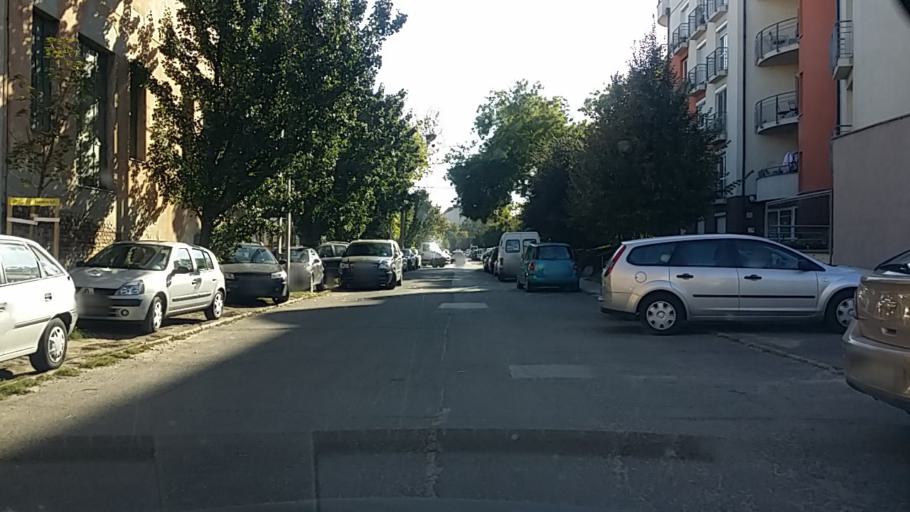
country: HU
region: Budapest
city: Budapest XI. keruelet
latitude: 47.4707
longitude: 19.0242
